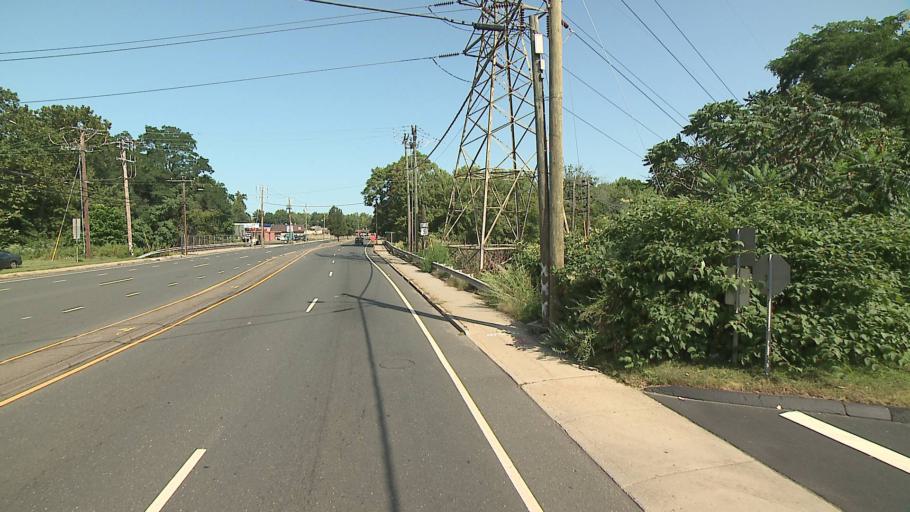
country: US
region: Connecticut
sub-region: Hartford County
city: East Hartford
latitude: 41.7610
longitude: -72.6450
